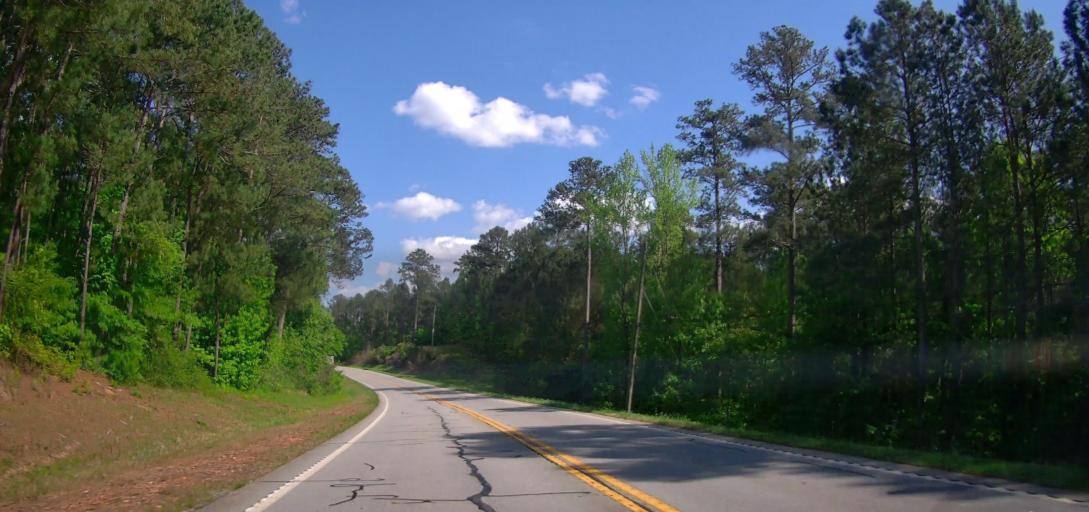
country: US
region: Georgia
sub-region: Greene County
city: Greensboro
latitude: 33.5767
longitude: -83.2633
